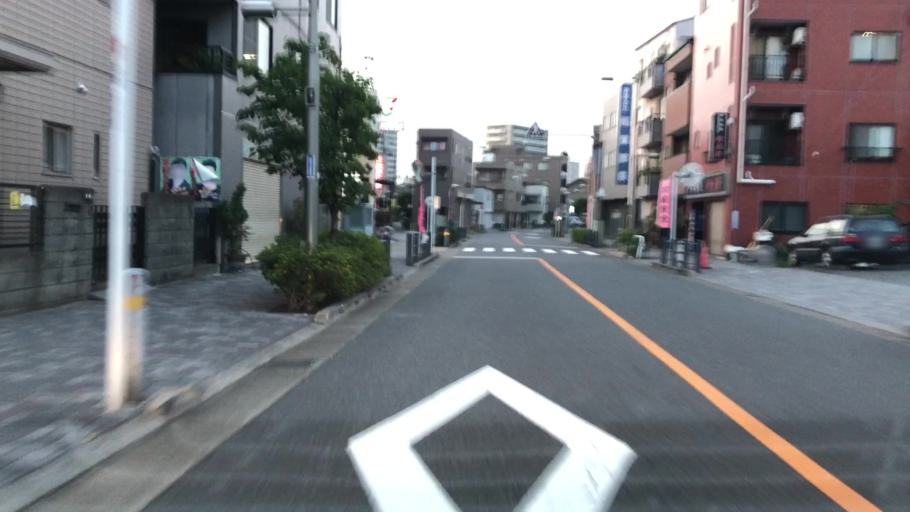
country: JP
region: Saitama
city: Soka
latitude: 35.7417
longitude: 139.7743
